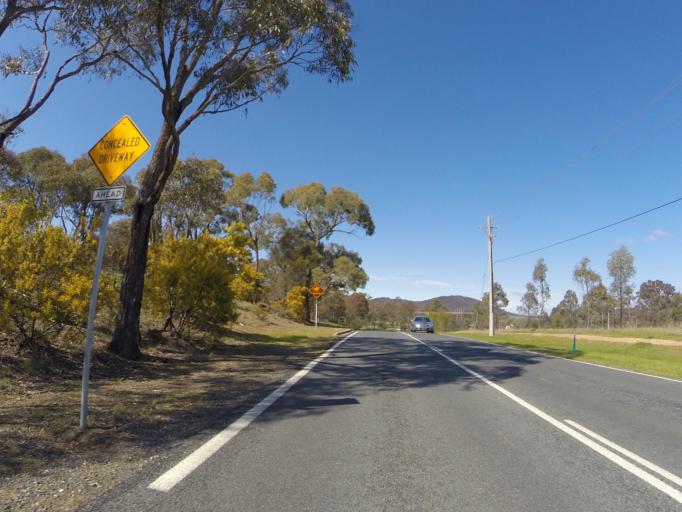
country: AU
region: Australian Capital Territory
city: Canberra
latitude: -35.2368
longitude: 149.1663
